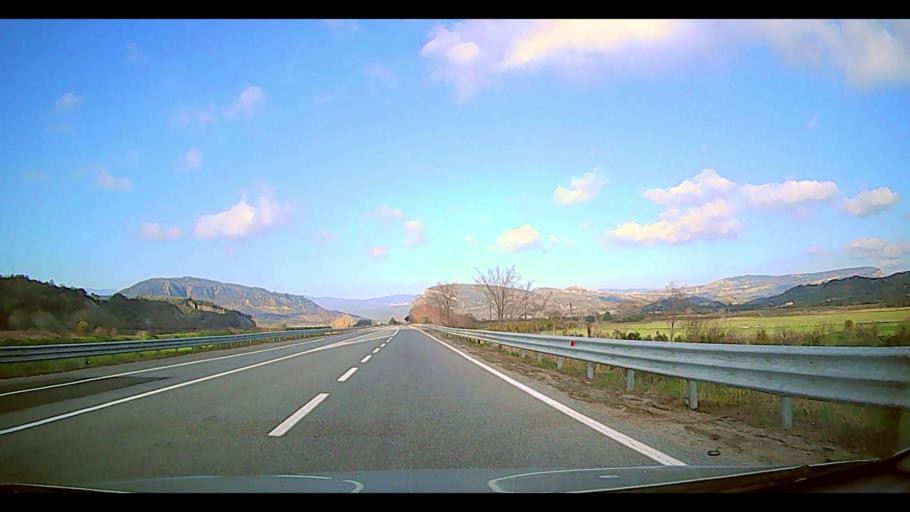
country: IT
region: Calabria
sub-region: Provincia di Crotone
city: Santa Severina
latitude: 39.1757
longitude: 16.9320
